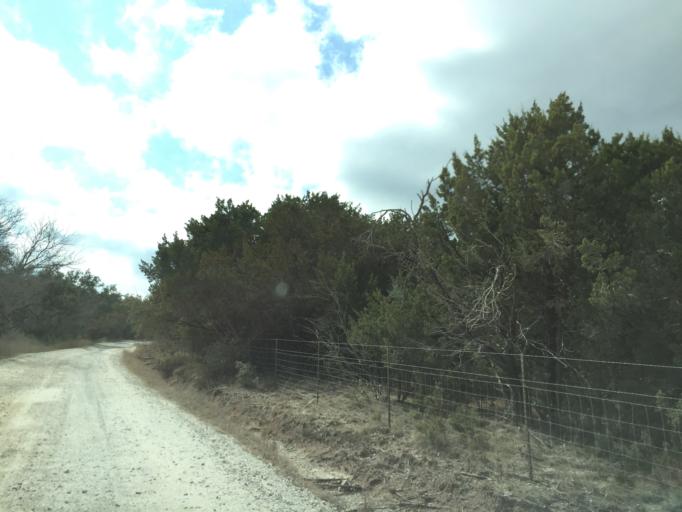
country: US
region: Texas
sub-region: Travis County
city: Briarcliff
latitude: 30.3850
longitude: -98.0947
